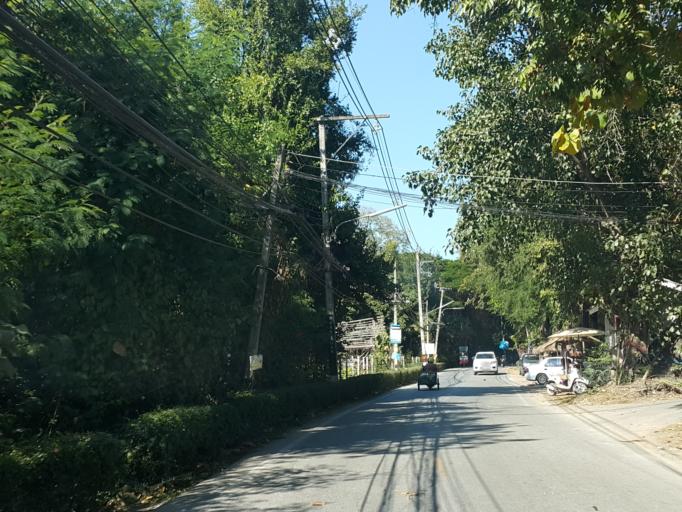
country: TH
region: Chiang Mai
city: San Sai
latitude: 18.8507
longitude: 98.9870
